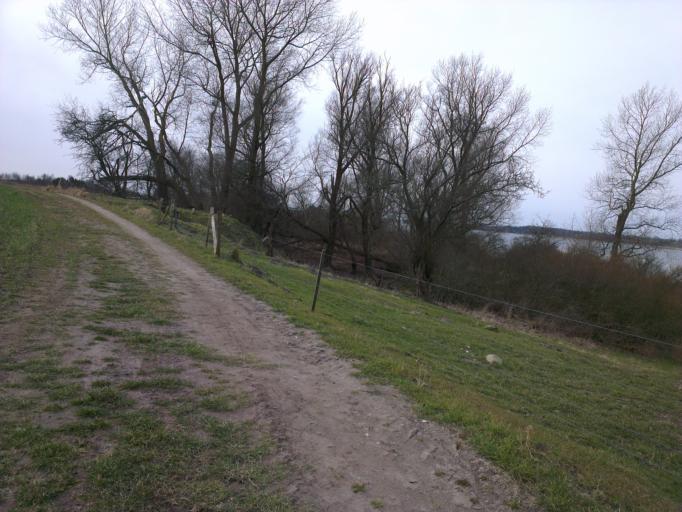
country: DK
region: Zealand
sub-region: Lejre Kommune
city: Ejby
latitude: 55.7765
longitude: 11.8627
